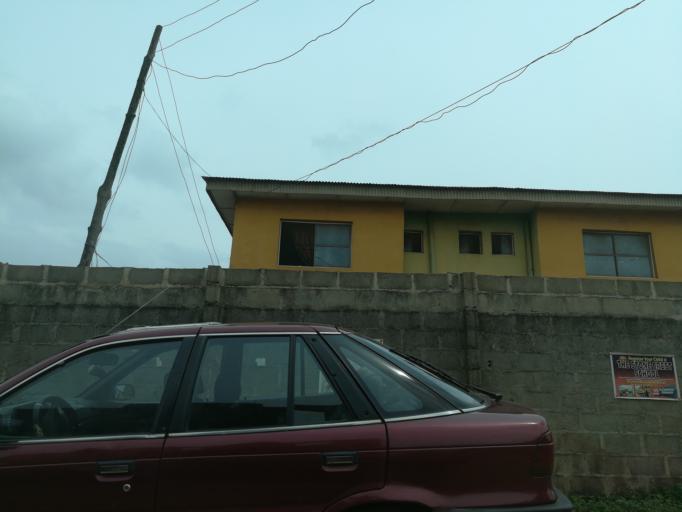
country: NG
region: Lagos
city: Ojota
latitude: 6.6057
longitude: 3.4143
